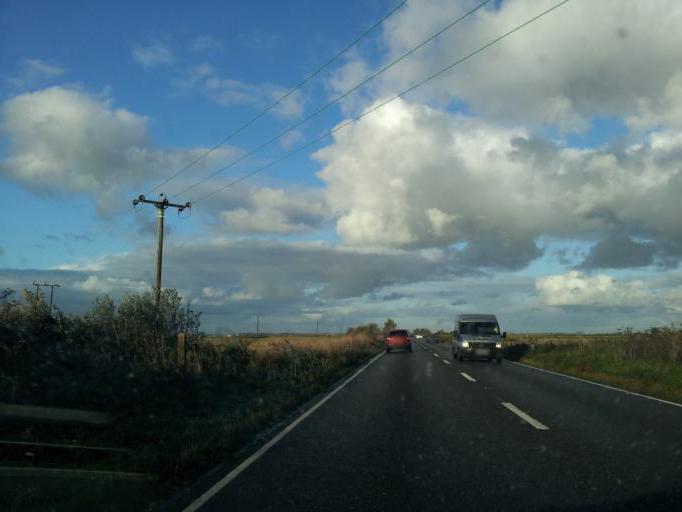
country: GB
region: England
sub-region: Norfolk
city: Great Yarmouth
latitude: 52.6201
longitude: 1.7036
